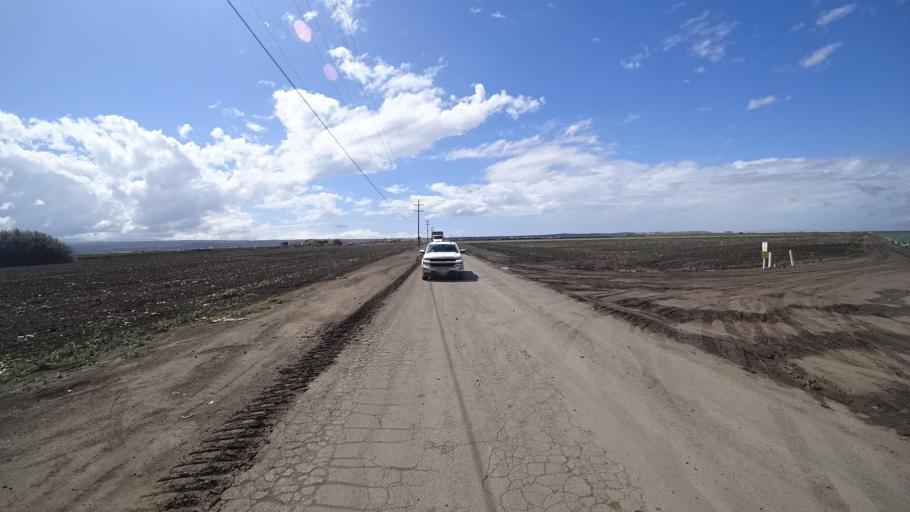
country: US
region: California
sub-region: Monterey County
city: Boronda
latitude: 36.6959
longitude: -121.7063
